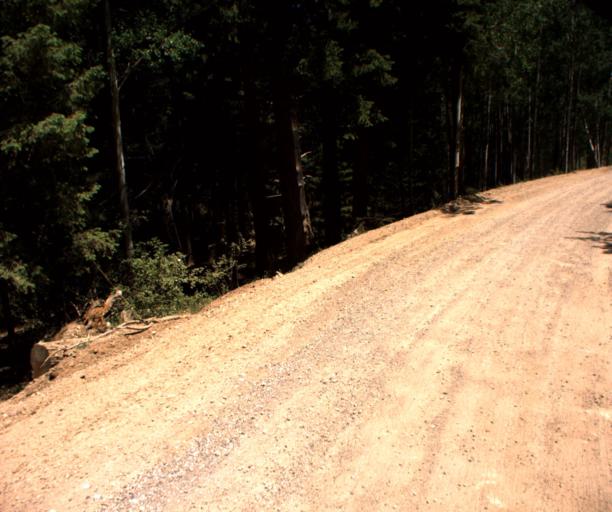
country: US
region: Arizona
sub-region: Graham County
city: Swift Trail Junction
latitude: 32.6932
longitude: -109.9048
